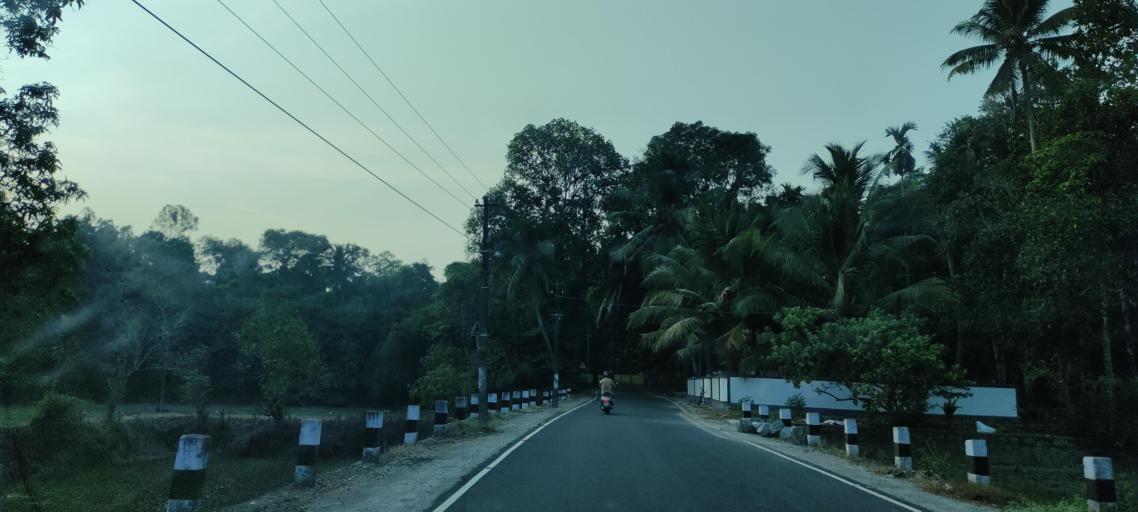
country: IN
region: Kerala
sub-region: Alappuzha
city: Mavelikara
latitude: 9.2779
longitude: 76.5554
